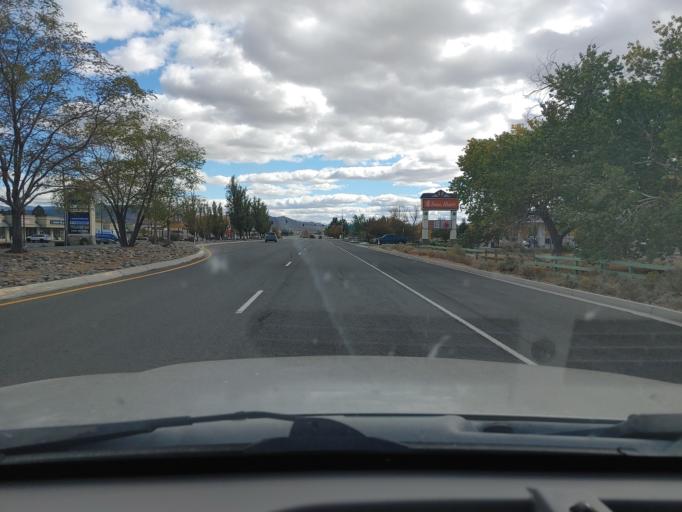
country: US
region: Nevada
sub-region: Carson City
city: Carson City
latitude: 39.1925
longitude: -119.7744
